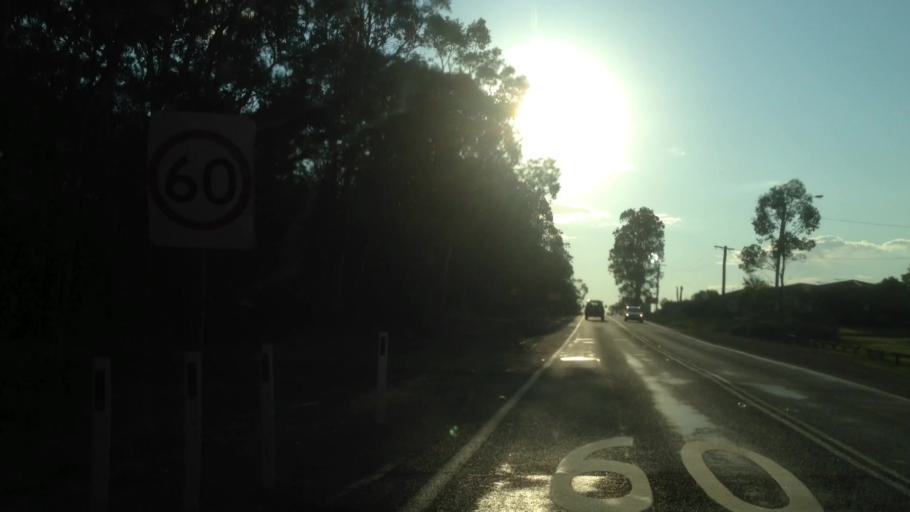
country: AU
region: New South Wales
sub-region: Cessnock
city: Kurri Kurri
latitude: -32.8284
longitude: 151.4927
